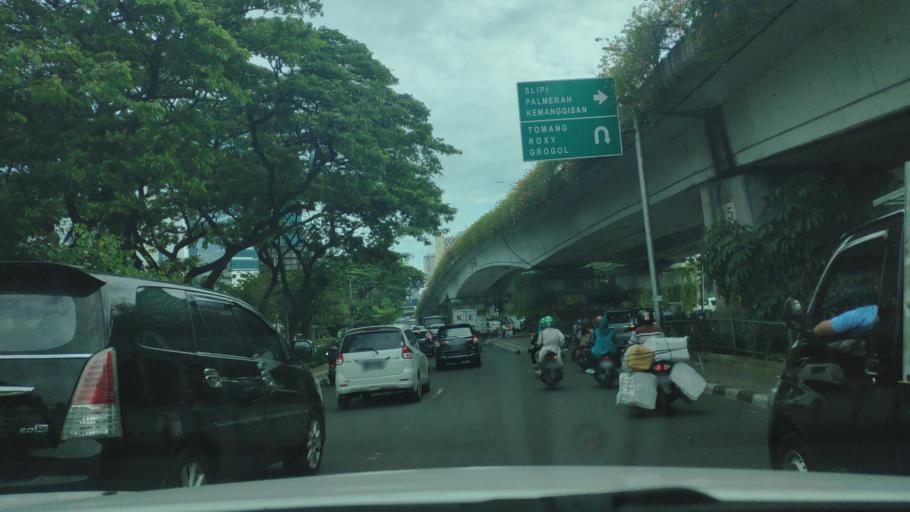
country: ID
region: Jakarta Raya
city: Jakarta
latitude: -6.1815
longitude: 106.8135
